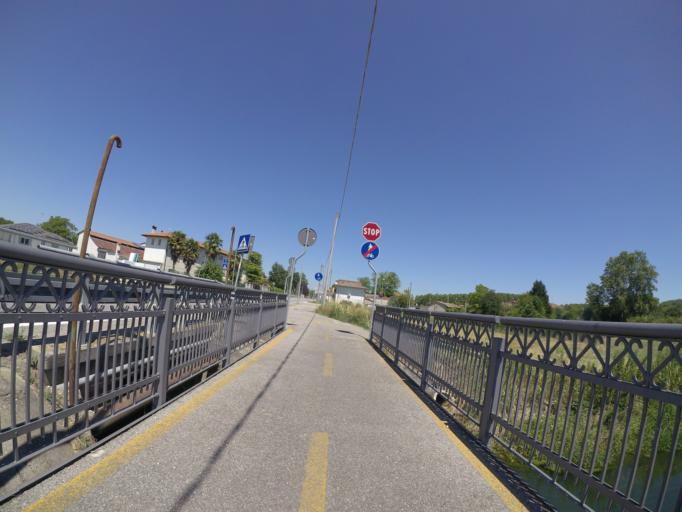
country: IT
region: Friuli Venezia Giulia
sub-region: Provincia di Udine
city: Teor
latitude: 45.8510
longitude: 13.0467
